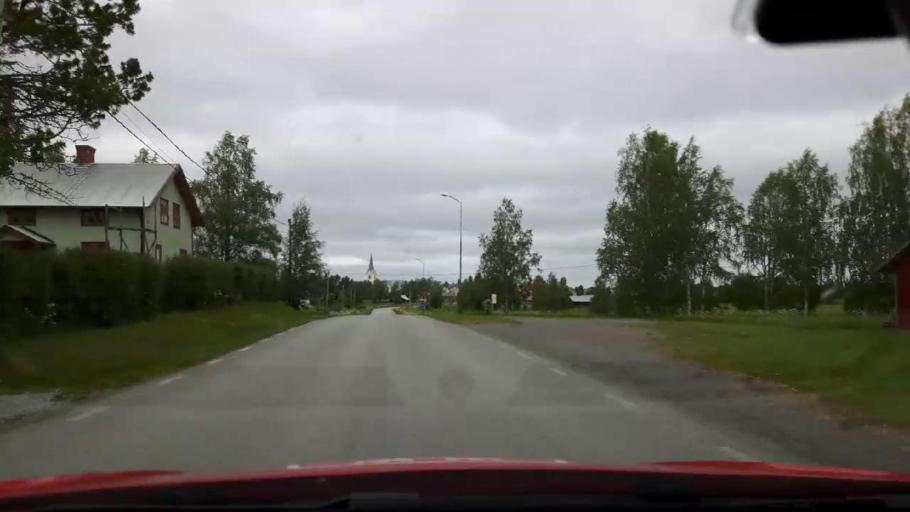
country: SE
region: Jaemtland
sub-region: OEstersunds Kommun
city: Lit
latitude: 63.6697
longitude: 15.1005
